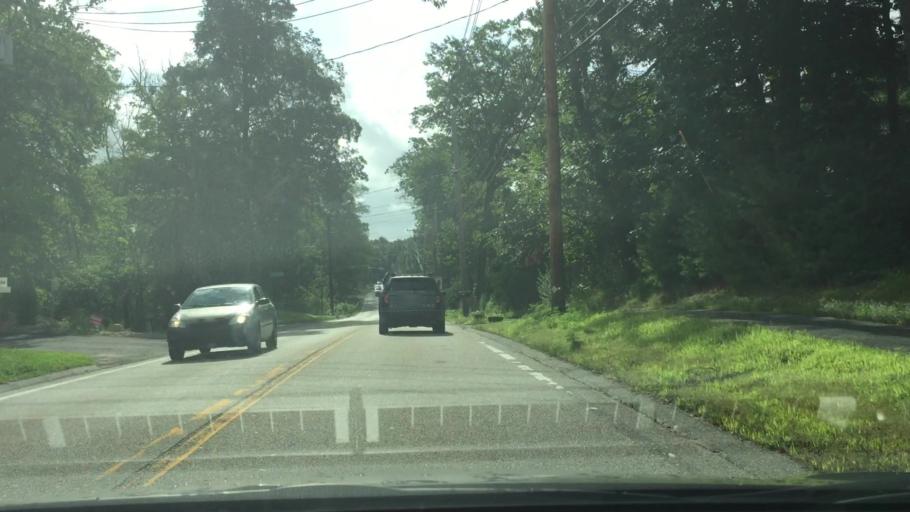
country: US
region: Massachusetts
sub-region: Middlesex County
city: Stow
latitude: 42.4816
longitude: -71.5097
